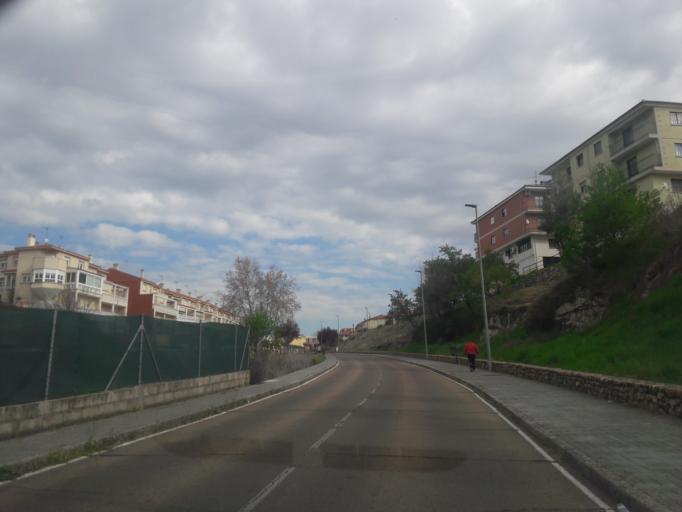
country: ES
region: Castille and Leon
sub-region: Provincia de Salamanca
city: Ciudad Rodrigo
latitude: 40.5938
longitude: -6.5257
